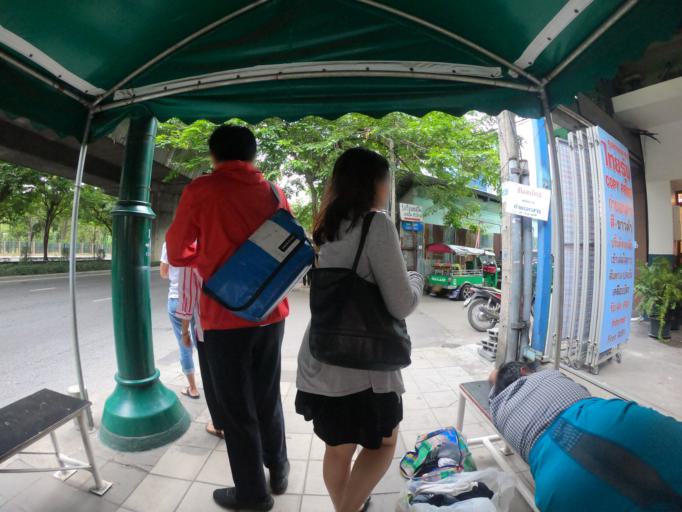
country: TH
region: Bangkok
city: Chatuchak
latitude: 13.8272
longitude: 100.5534
